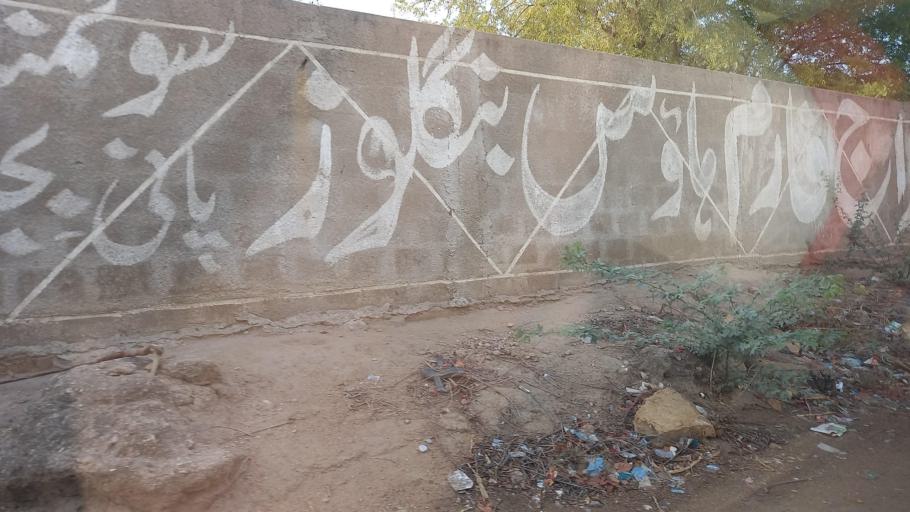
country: PK
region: Sindh
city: Malir Cantonment
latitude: 25.1169
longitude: 67.1918
